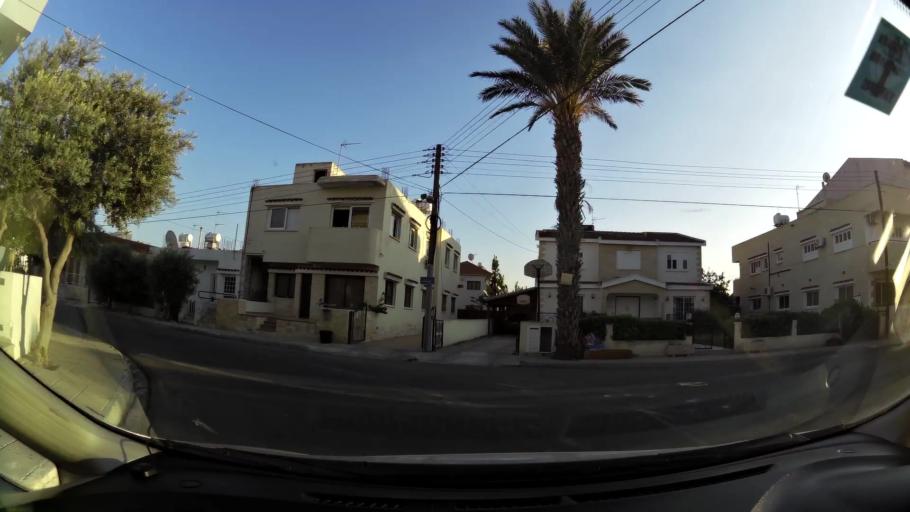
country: CY
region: Larnaka
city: Larnaca
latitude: 34.9188
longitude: 33.5909
